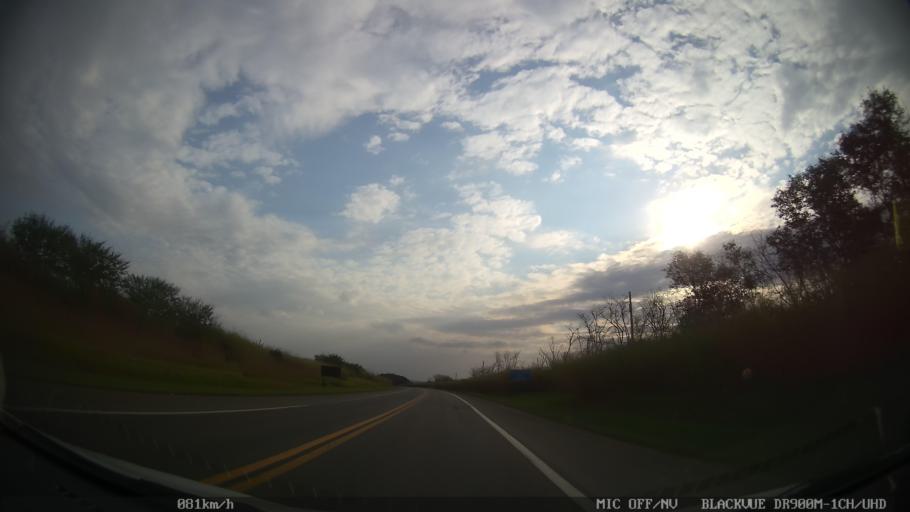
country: BR
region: Sao Paulo
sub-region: Cosmopolis
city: Cosmopolis
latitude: -22.6121
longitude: -47.2341
